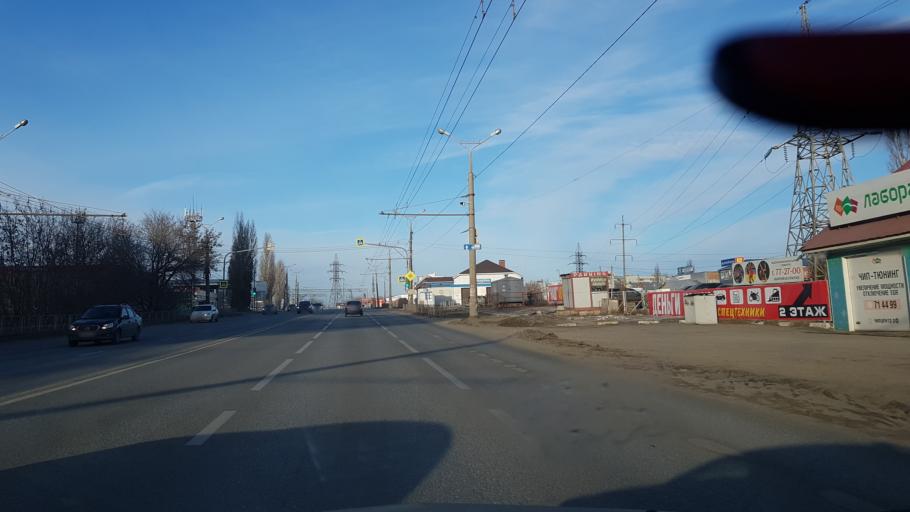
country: RU
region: Samara
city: Tol'yatti
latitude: 53.5328
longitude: 49.3961
